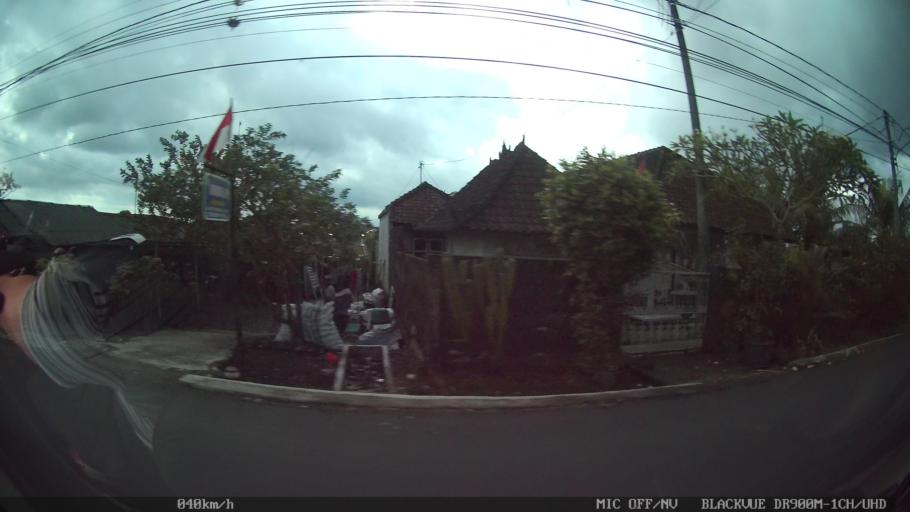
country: ID
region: Bali
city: Banjar Tegal Belodan
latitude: -8.5423
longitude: 115.1170
